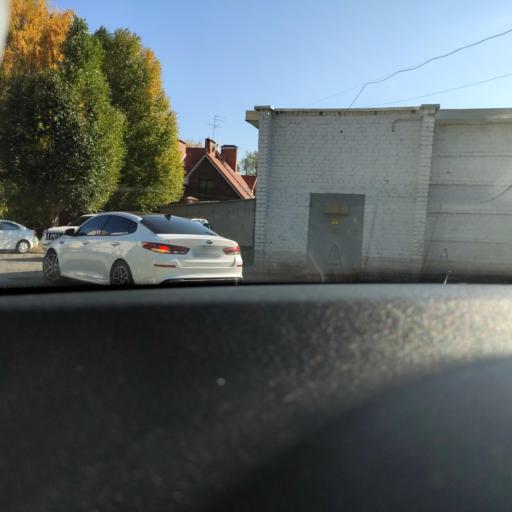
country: RU
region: Samara
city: Samara
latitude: 53.2743
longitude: 50.1933
